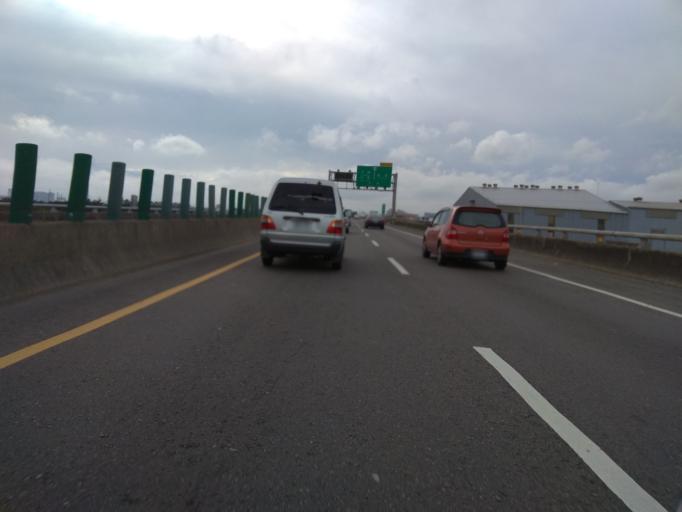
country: TW
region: Taiwan
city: Daxi
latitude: 24.9216
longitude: 121.2224
